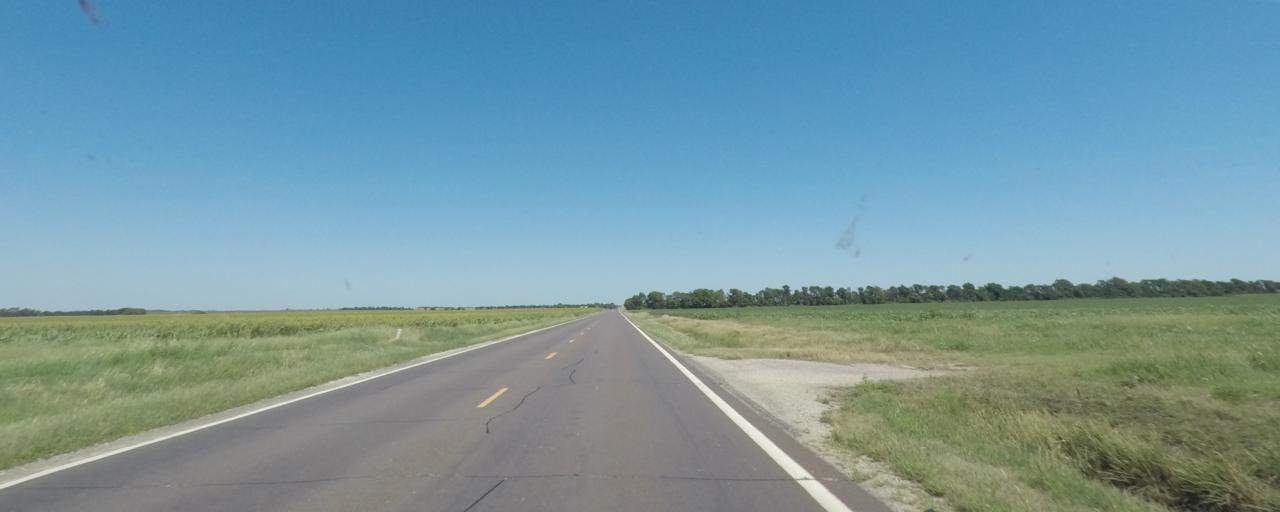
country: US
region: Kansas
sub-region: Sumner County
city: Wellington
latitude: 37.1768
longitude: -97.4020
